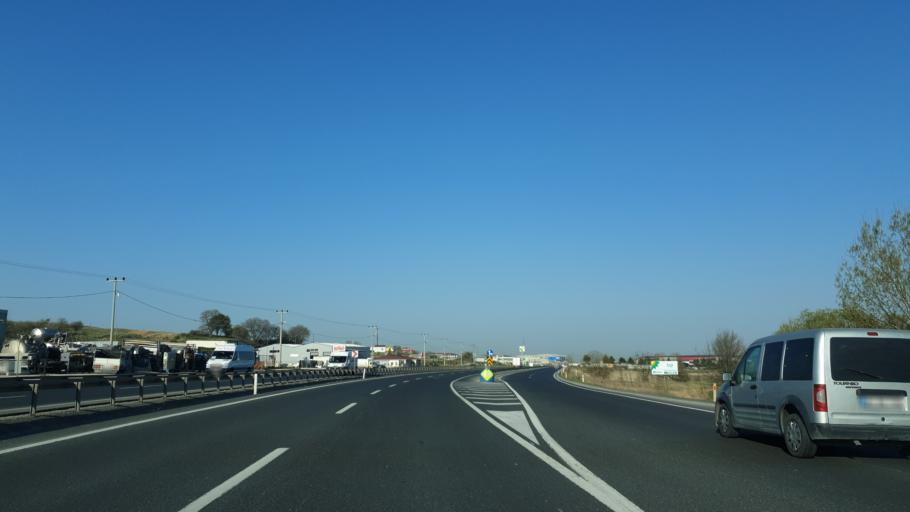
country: TR
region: Tekirdag
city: Cerkezkoey
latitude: 41.2654
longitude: 27.9514
